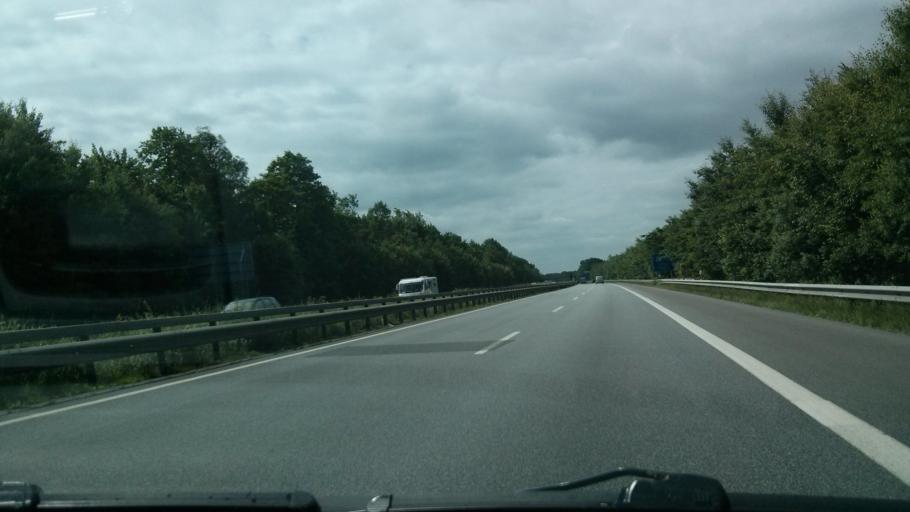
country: DE
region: Lower Saxony
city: Loxstedt
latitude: 53.4557
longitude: 8.5916
